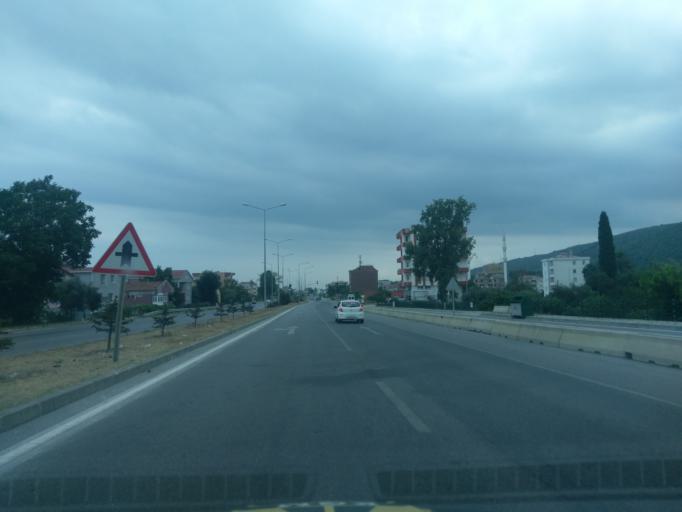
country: TR
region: Samsun
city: Taflan
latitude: 41.4049
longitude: 36.1836
